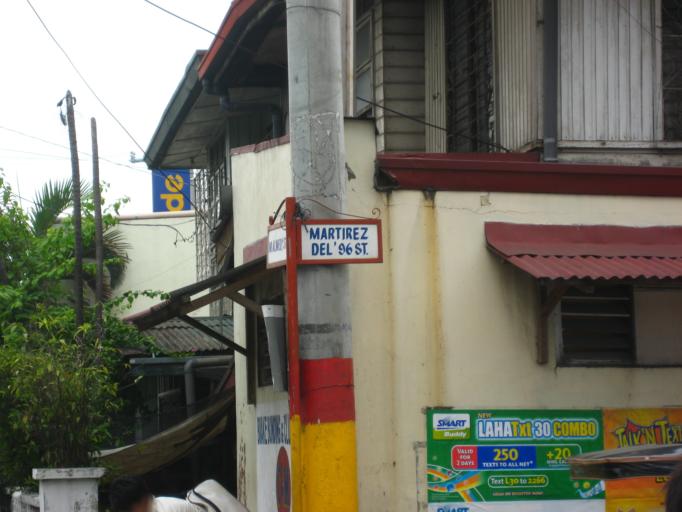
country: PH
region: Calabarzon
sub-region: Province of Rizal
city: Pateros
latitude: 14.5409
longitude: 121.0672
